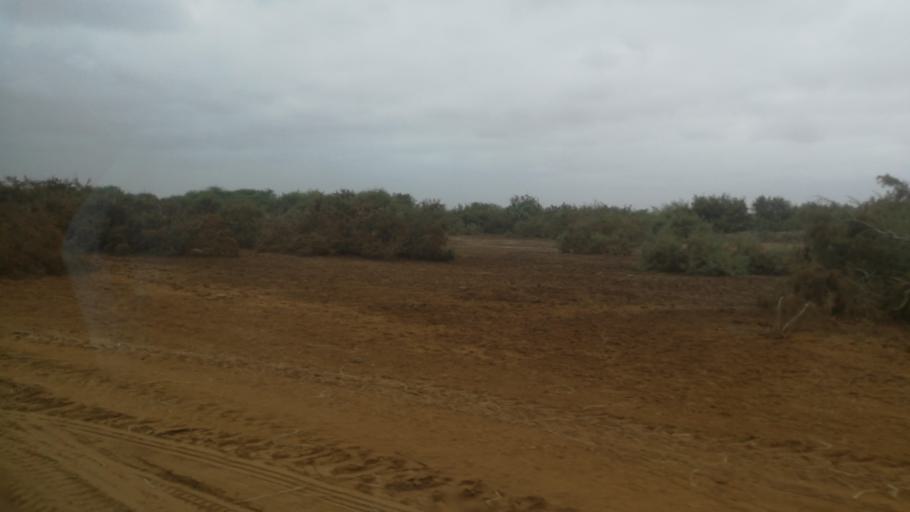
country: SN
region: Saint-Louis
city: Rosso
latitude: 16.2794
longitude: -16.1666
